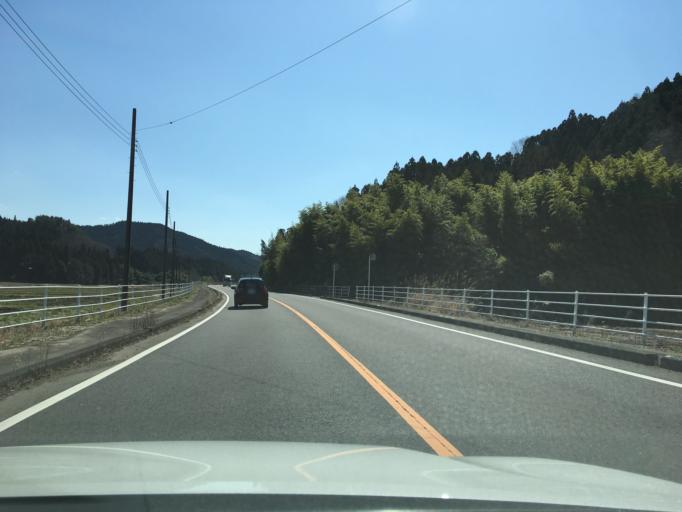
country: JP
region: Tochigi
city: Kuroiso
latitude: 37.0153
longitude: 140.1774
